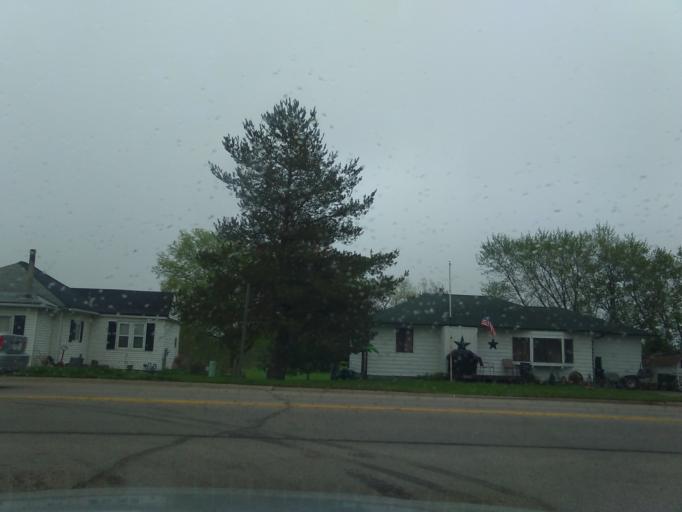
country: US
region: Nebraska
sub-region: Wayne County
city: Wayne
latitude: 42.2255
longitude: -97.0179
